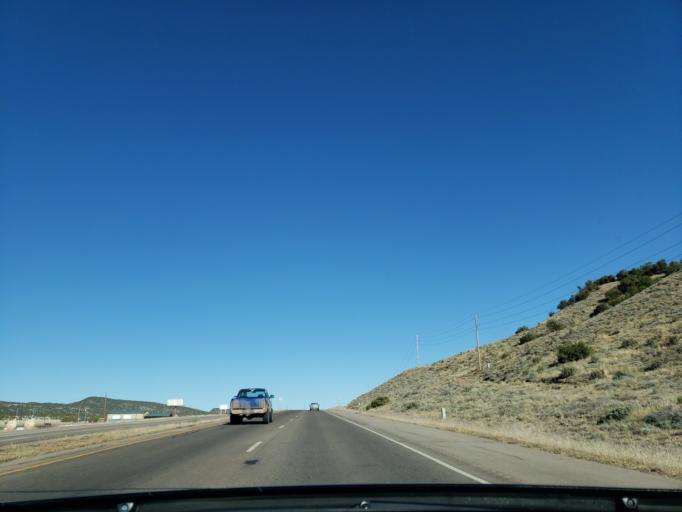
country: US
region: Colorado
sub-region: Fremont County
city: Lincoln Park
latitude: 38.4486
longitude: -105.1726
